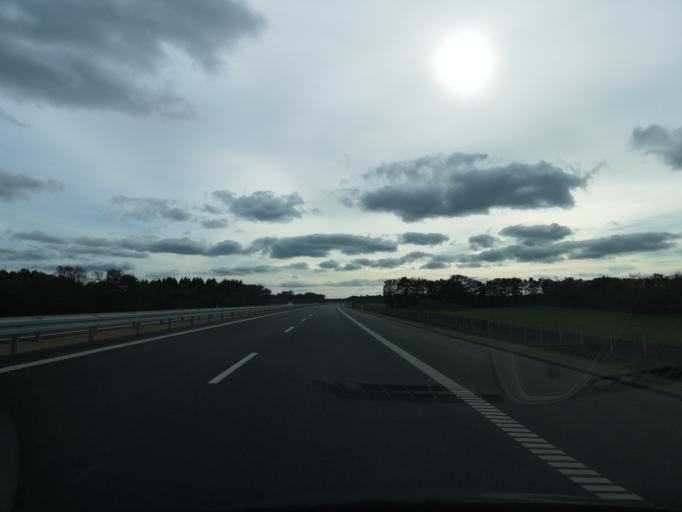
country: DK
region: Central Jutland
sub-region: Herning Kommune
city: Avlum
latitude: 56.3242
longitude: 8.7340
